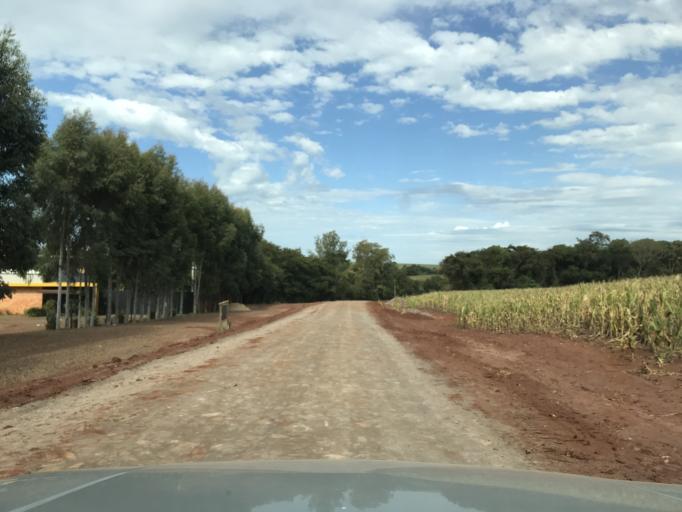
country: BR
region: Parana
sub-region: Palotina
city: Palotina
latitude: -24.3004
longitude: -53.8110
